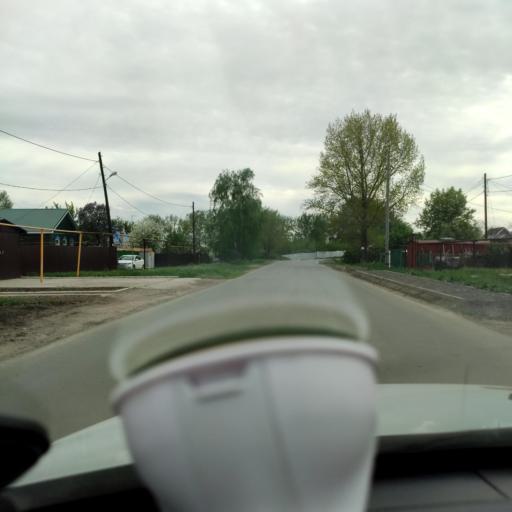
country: RU
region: Samara
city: Smyshlyayevka
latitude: 53.2169
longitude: 50.3326
